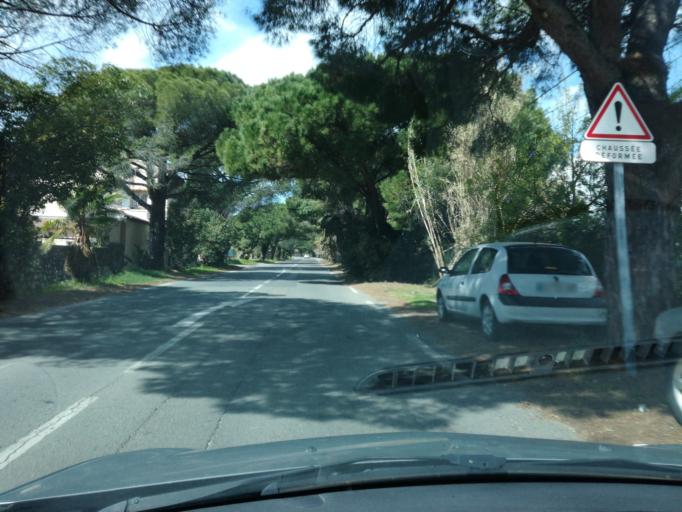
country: FR
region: Provence-Alpes-Cote d'Azur
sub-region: Departement du Var
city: Hyeres
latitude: 43.1150
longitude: 6.1554
